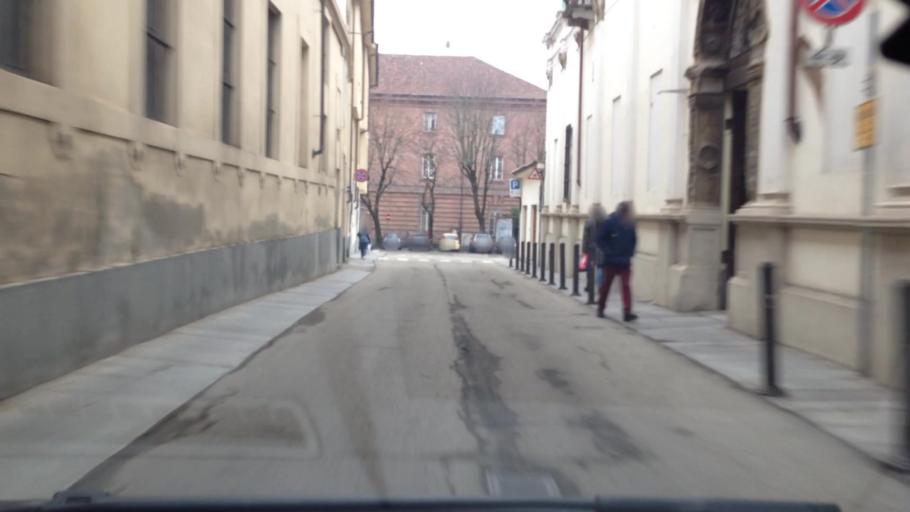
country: IT
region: Piedmont
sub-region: Provincia di Asti
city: Asti
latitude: 44.8982
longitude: 8.1980
